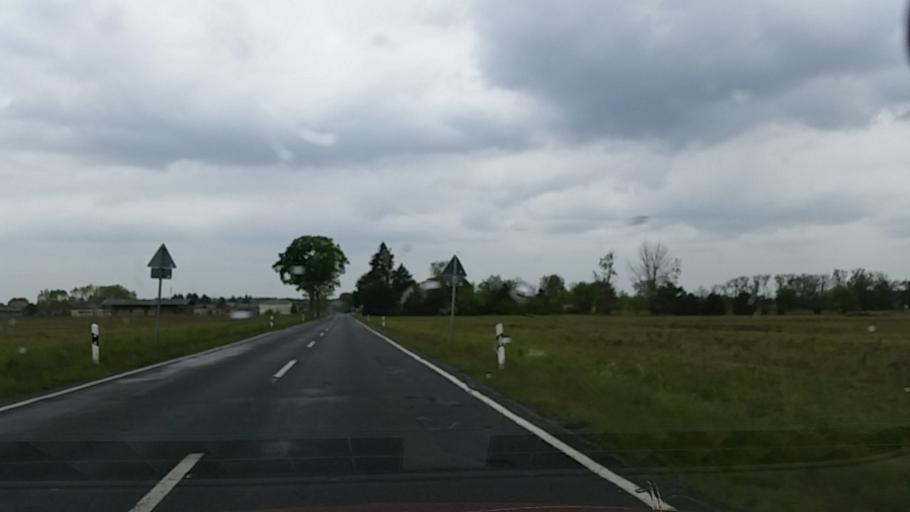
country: DE
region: Brandenburg
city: Spreenhagen
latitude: 52.3378
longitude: 13.8912
